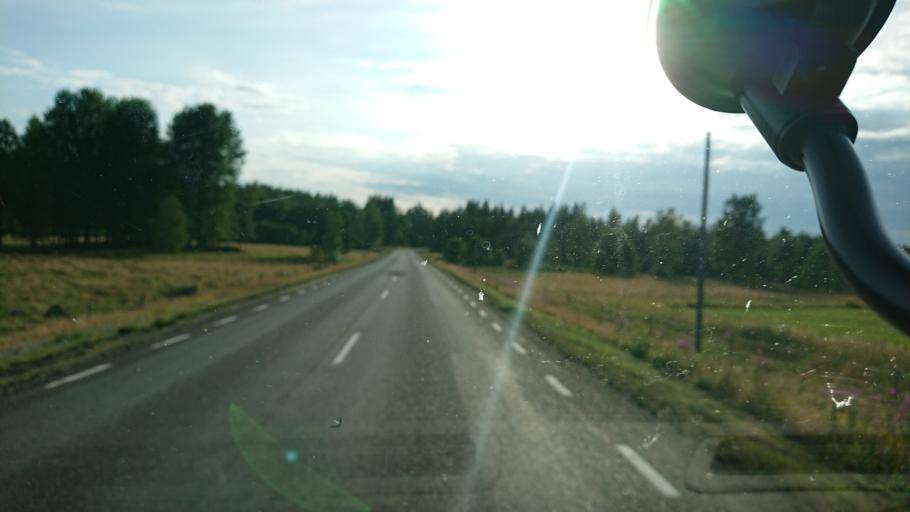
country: SE
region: Kronoberg
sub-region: Vaxjo Kommun
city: Braas
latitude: 57.0227
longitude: 15.0181
